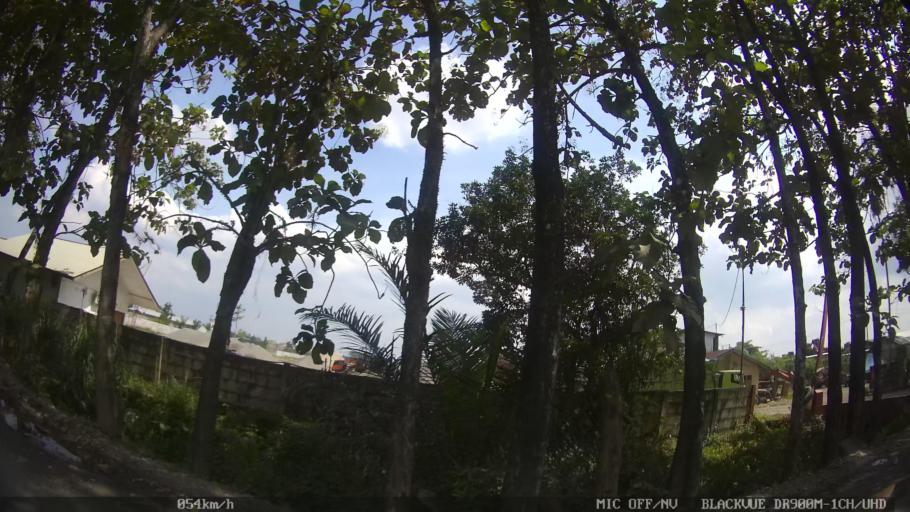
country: ID
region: North Sumatra
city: Binjai
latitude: 3.6350
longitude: 98.5318
